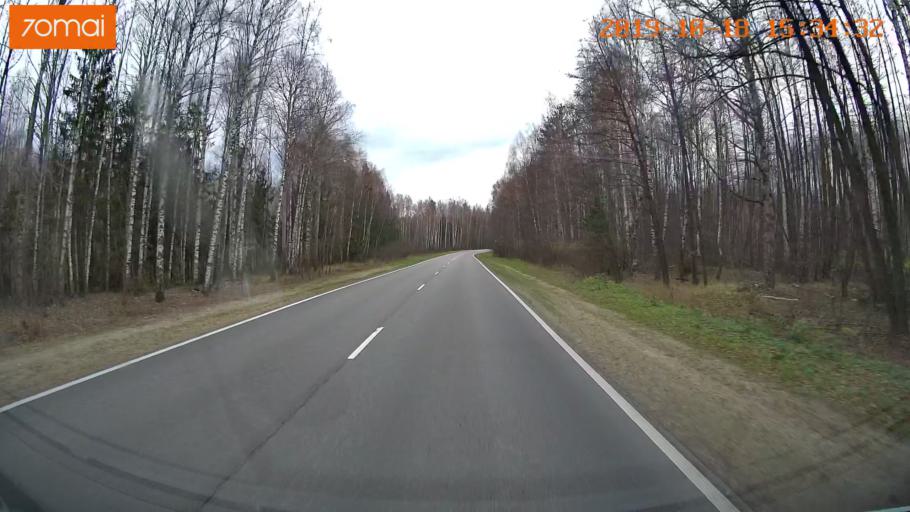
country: RU
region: Vladimir
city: Anopino
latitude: 55.8553
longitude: 40.6411
